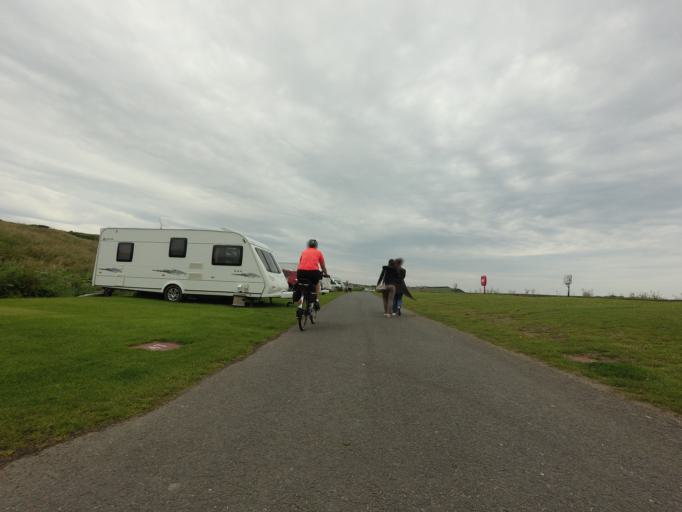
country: GB
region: Scotland
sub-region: Aberdeenshire
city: Whitehills
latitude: 57.6713
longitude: -2.5571
